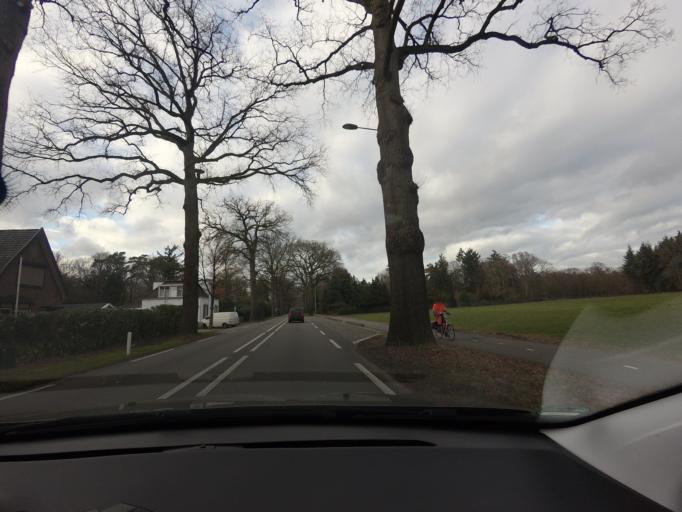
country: NL
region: Gelderland
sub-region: Gemeente Lochem
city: Eefde
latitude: 52.1830
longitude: 6.2138
